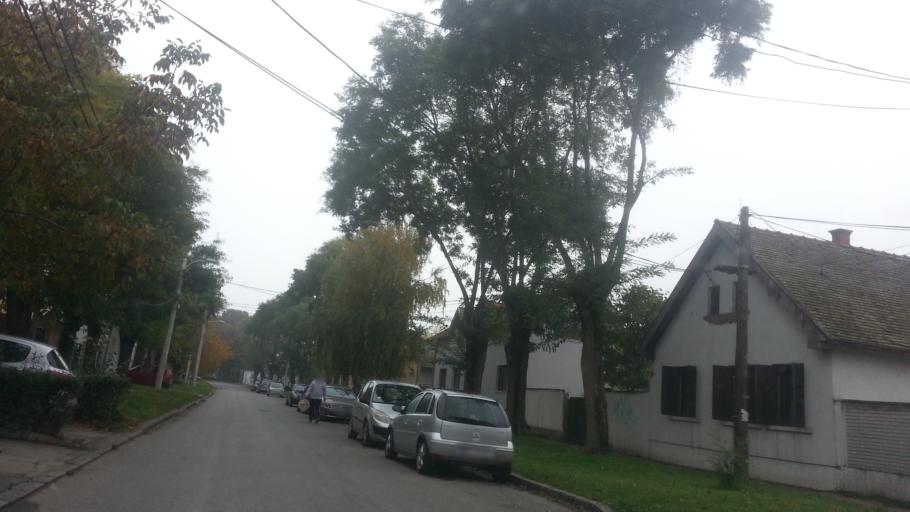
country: RS
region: Central Serbia
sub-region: Belgrade
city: Zemun
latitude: 44.8513
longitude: 20.4023
